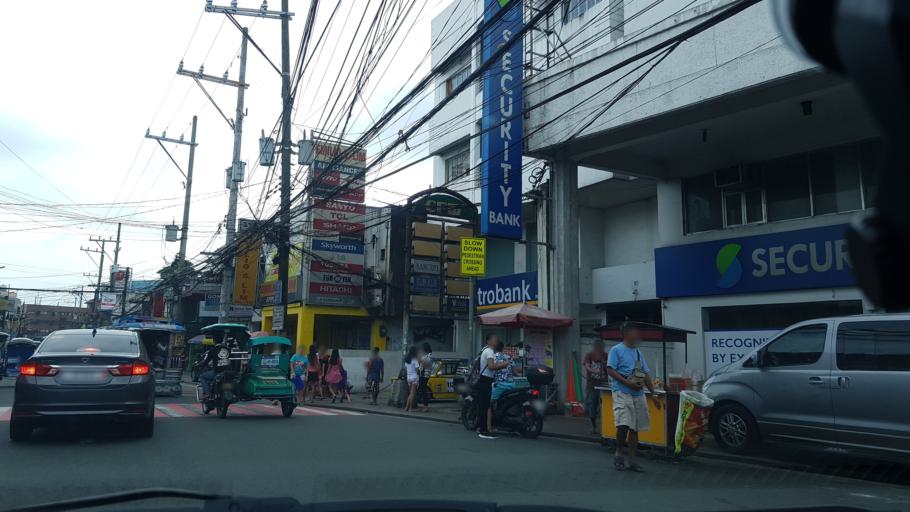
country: PH
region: Calabarzon
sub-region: Province of Rizal
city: Pateros
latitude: 14.5645
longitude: 121.0758
